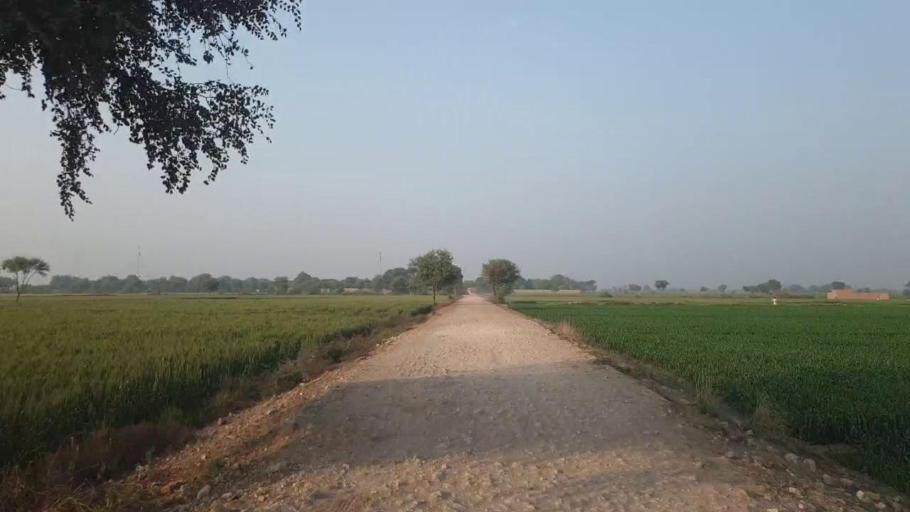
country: PK
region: Sindh
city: Bhit Shah
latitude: 25.8093
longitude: 68.4769
